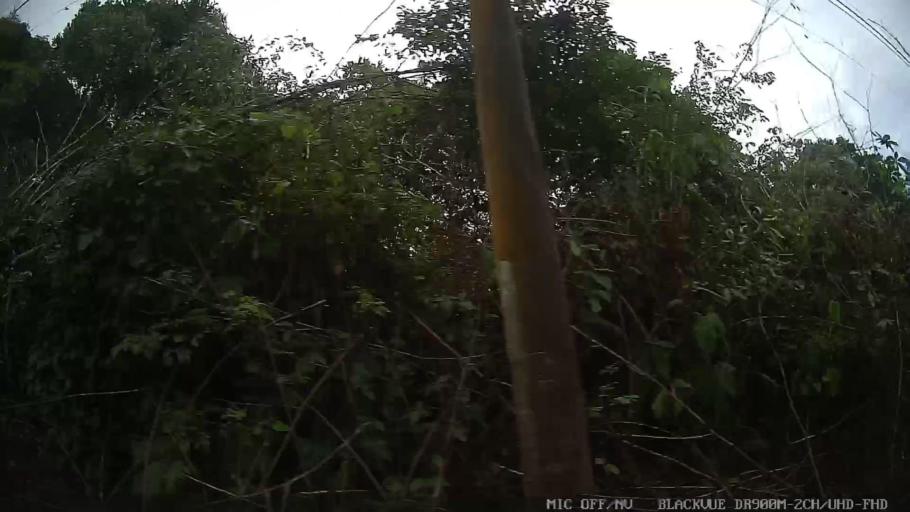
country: BR
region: Sao Paulo
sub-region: Iguape
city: Iguape
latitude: -24.6708
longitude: -47.4446
